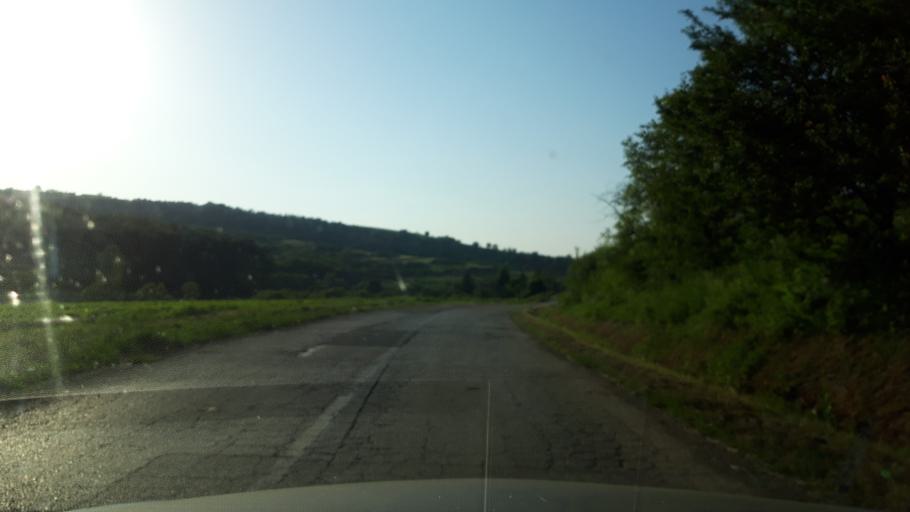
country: RS
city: Glozan
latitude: 45.1616
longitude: 19.5907
